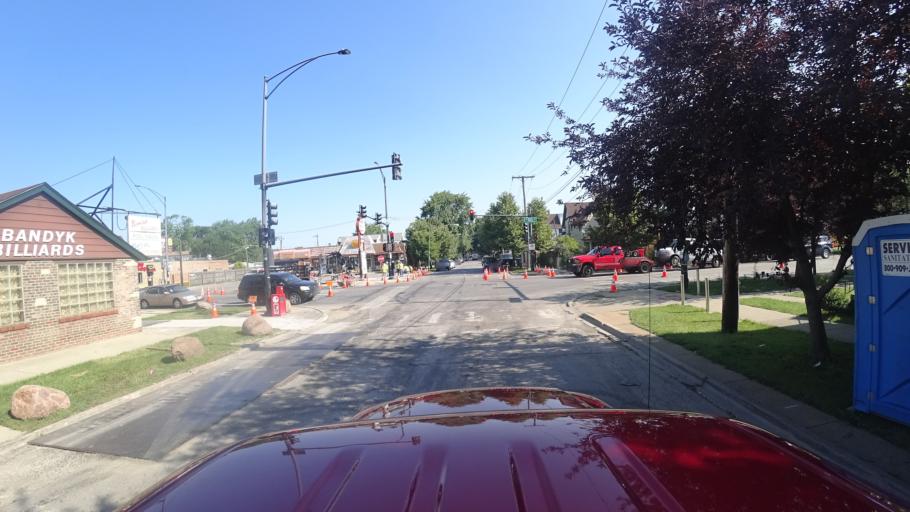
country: US
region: Illinois
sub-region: Cook County
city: Hometown
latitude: 41.7932
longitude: -87.7158
